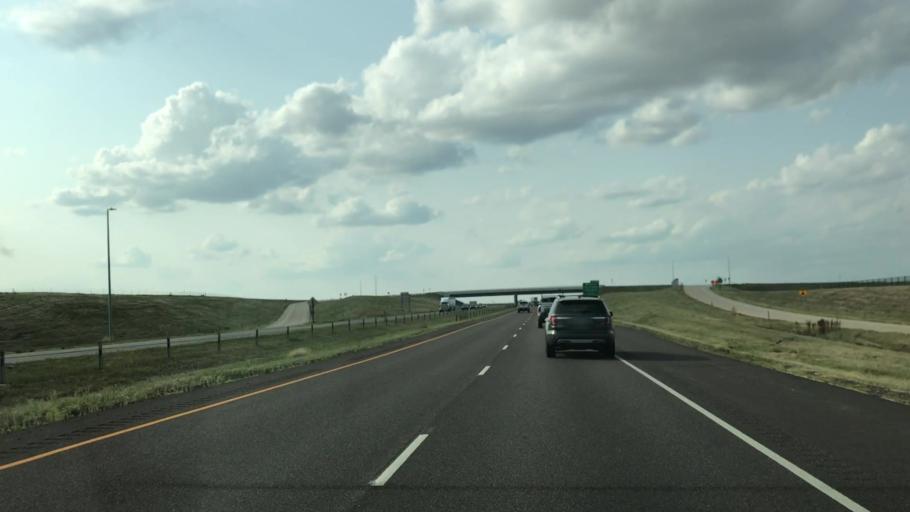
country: US
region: Colorado
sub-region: Adams County
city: Aurora
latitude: 39.8092
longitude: -104.7185
